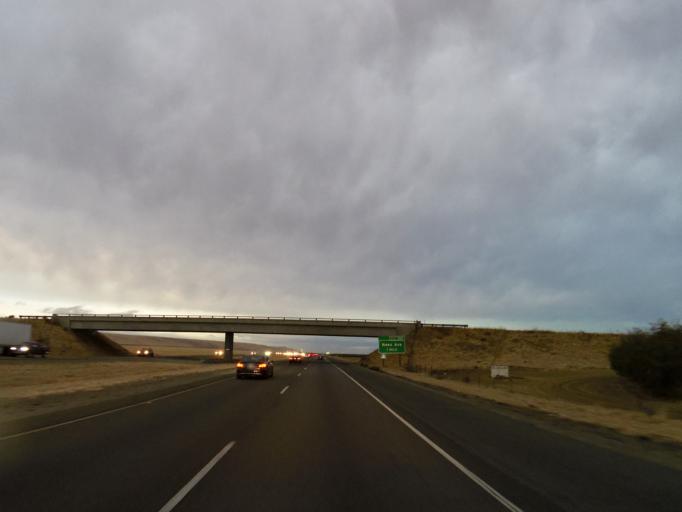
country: US
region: California
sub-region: Merced County
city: South Dos Palos
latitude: 36.8348
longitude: -120.7630
